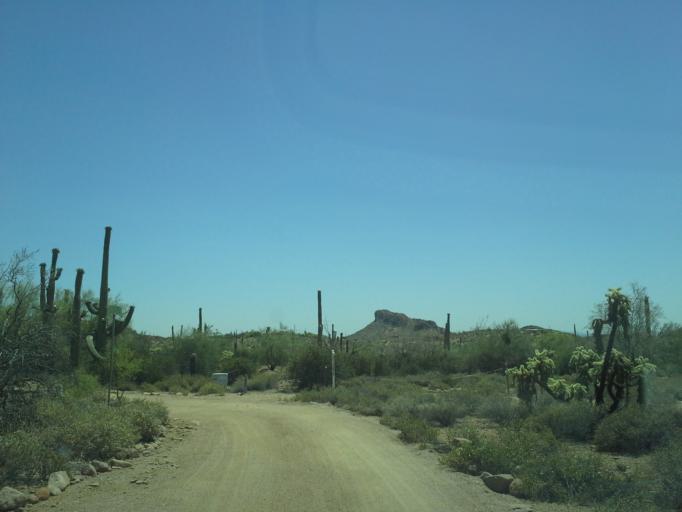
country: US
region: Arizona
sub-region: Pinal County
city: Apache Junction
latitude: 33.3919
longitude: -111.4368
